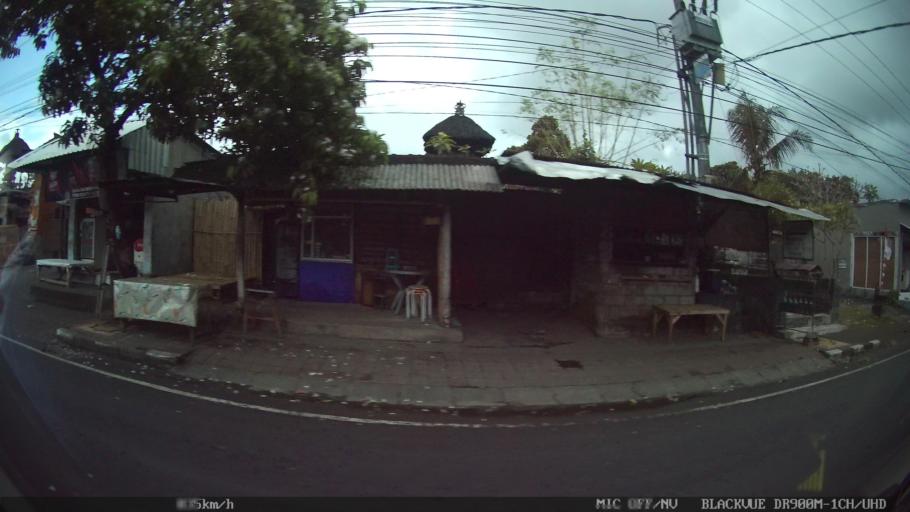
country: ID
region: Bali
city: Banjar Cemenggon
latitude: -8.5362
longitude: 115.1995
